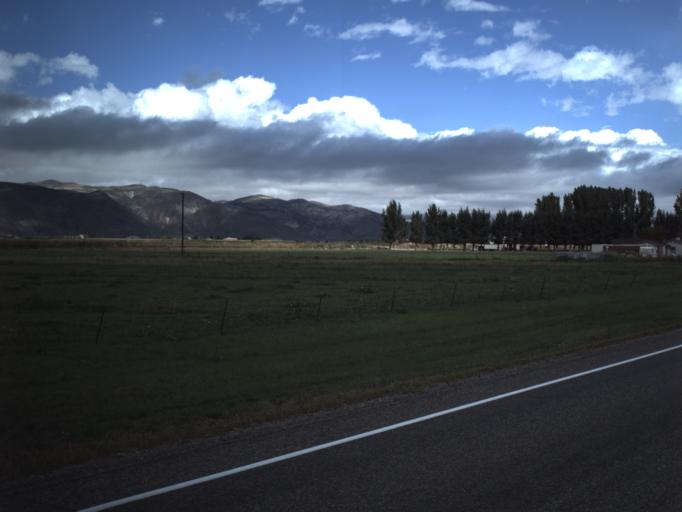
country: US
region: Utah
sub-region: Sevier County
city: Monroe
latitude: 38.6934
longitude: -112.1154
